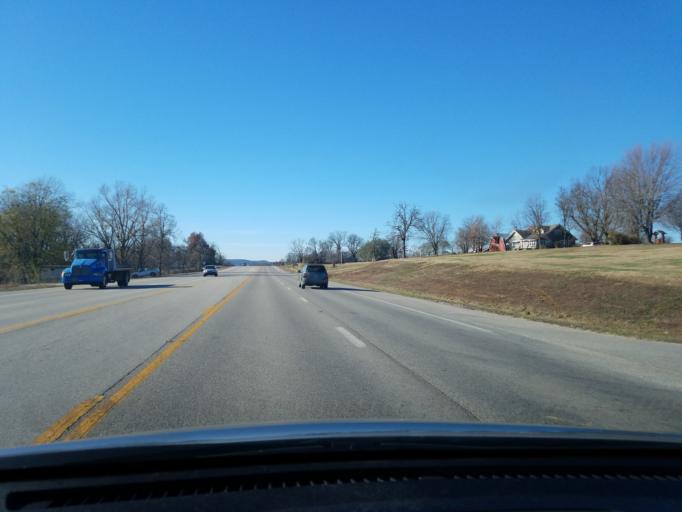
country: US
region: Arkansas
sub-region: Carroll County
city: Berryville
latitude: 36.3843
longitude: -93.6036
